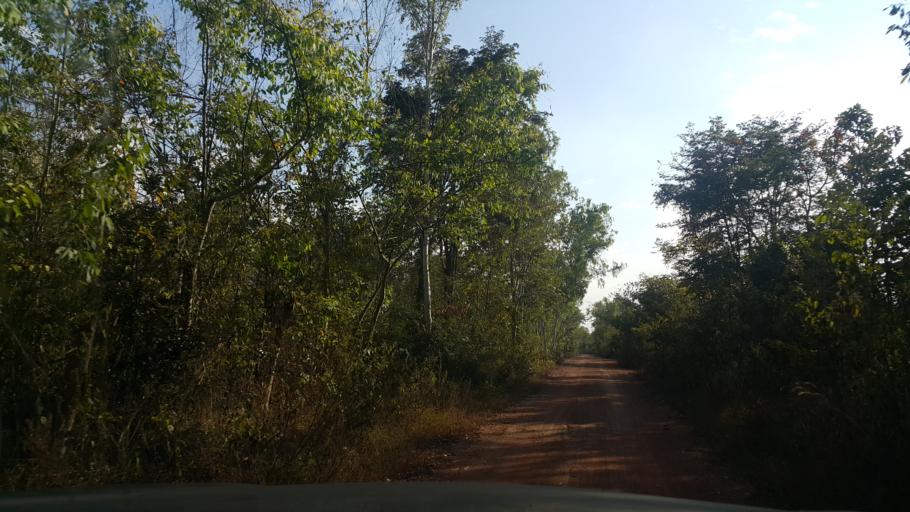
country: TH
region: Lampang
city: Hang Chat
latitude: 18.2797
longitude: 99.3571
